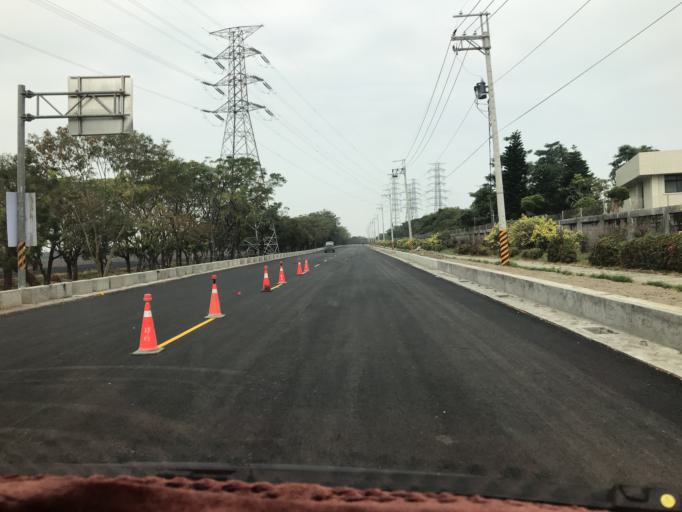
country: TW
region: Taiwan
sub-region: Pingtung
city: Pingtung
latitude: 22.4159
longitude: 120.6086
